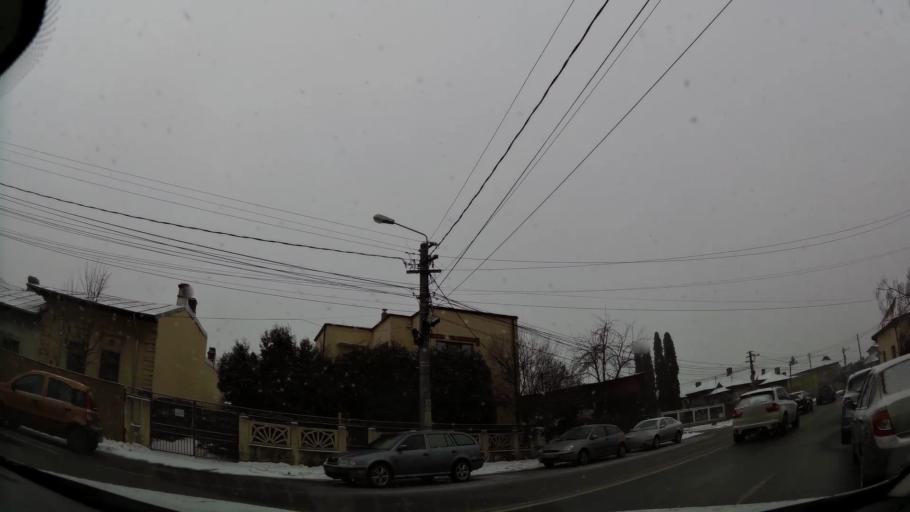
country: RO
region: Dambovita
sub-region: Municipiul Targoviste
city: Targoviste
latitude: 44.9356
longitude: 25.4512
